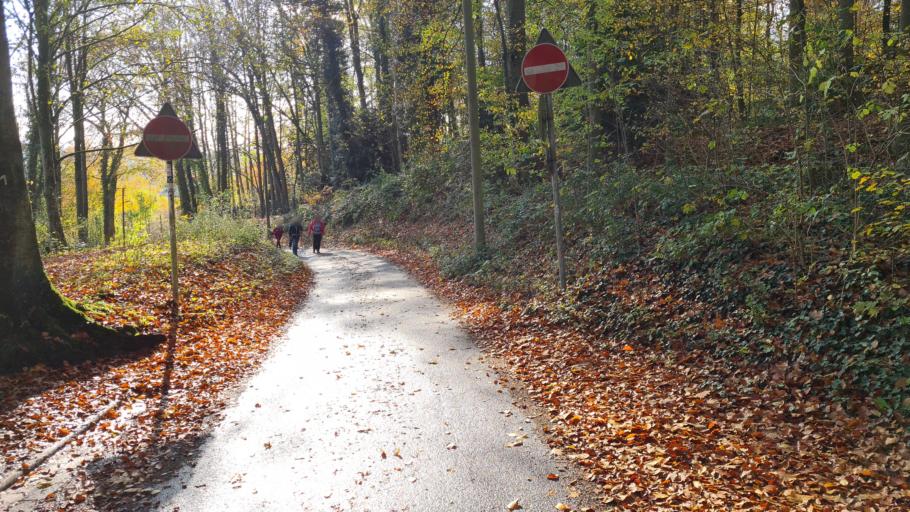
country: DE
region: North Rhine-Westphalia
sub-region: Regierungsbezirk Dusseldorf
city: Essen
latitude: 51.3916
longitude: 6.9932
